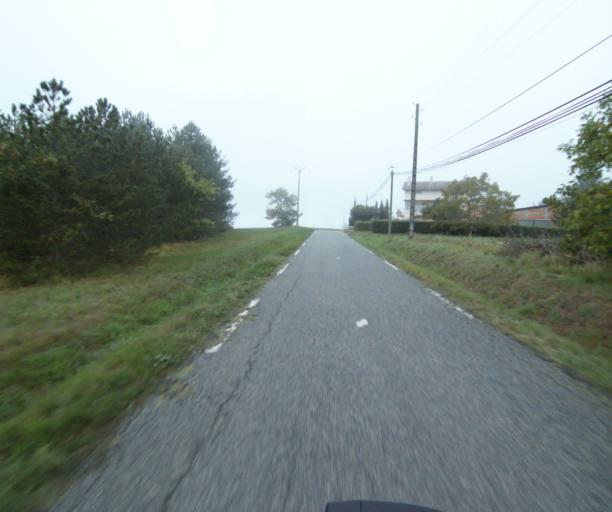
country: FR
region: Midi-Pyrenees
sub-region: Departement du Tarn-et-Garonne
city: Corbarieu
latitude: 43.9554
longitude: 1.3934
